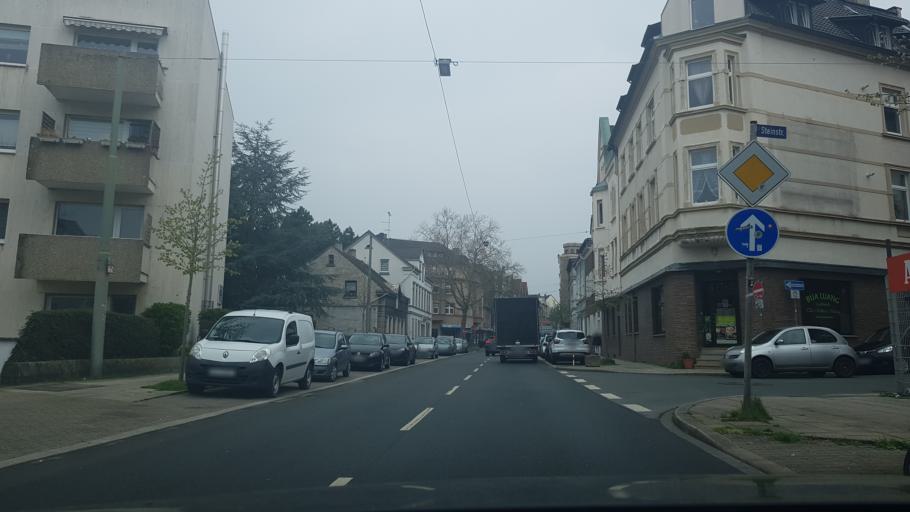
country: DE
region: North Rhine-Westphalia
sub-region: Regierungsbezirk Munster
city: Gelsenkirchen
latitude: 51.4786
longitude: 7.1400
